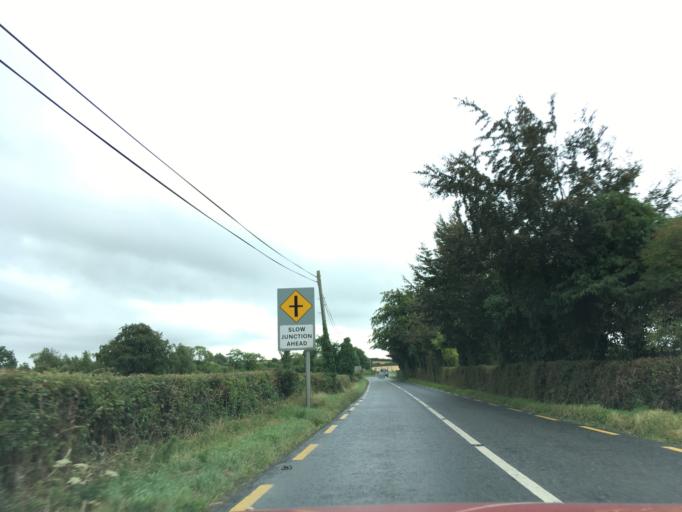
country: IE
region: Munster
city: Fethard
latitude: 52.4249
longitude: -7.7734
